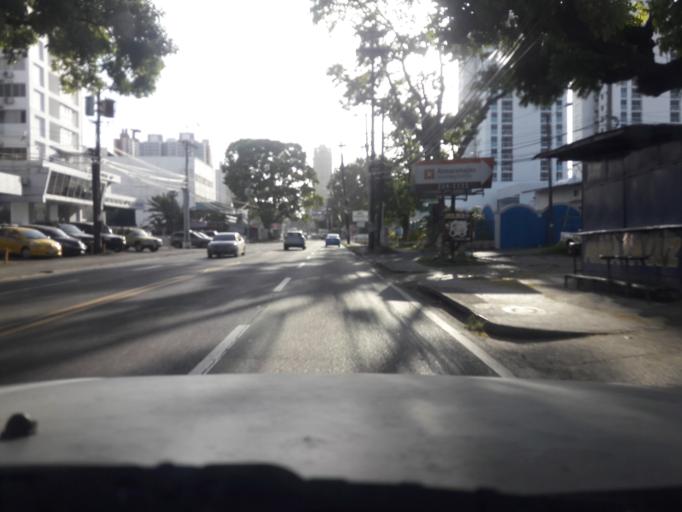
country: PA
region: Panama
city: Panama
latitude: 9.0107
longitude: -79.5047
